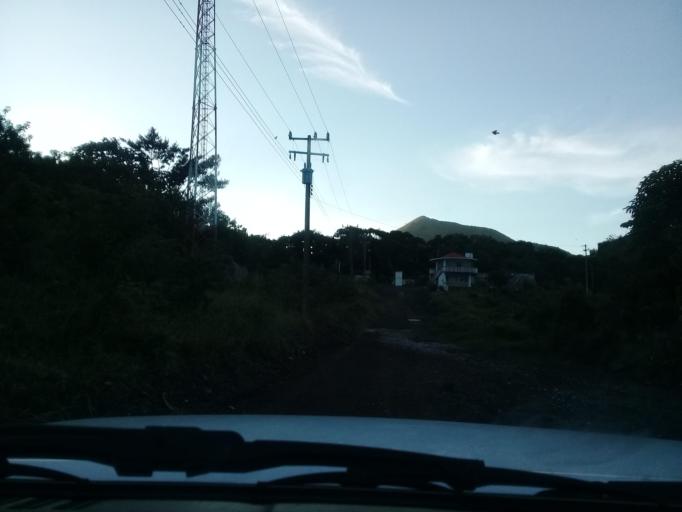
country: MX
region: Veracruz
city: Catemaco
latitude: 18.4374
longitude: -95.0873
